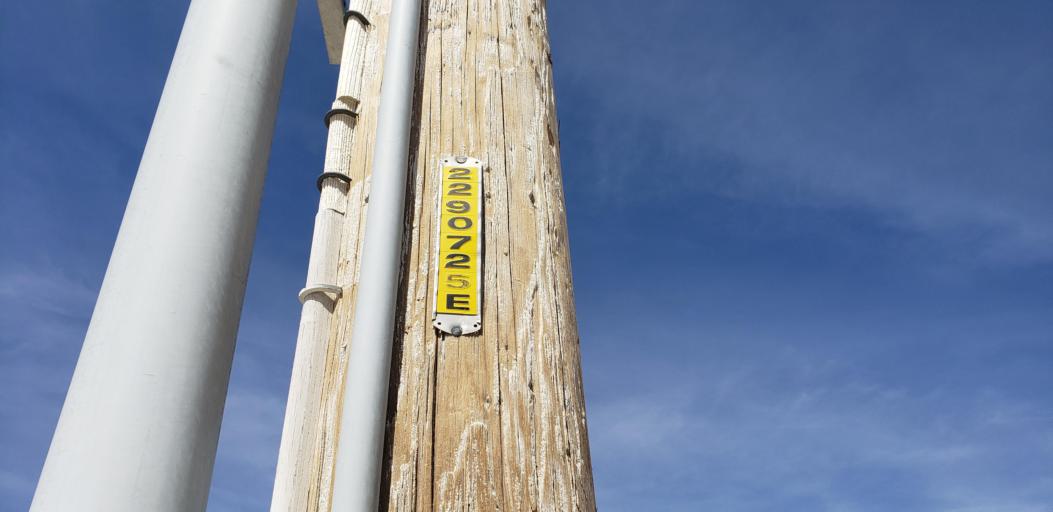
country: US
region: California
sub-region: San Bernardino County
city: Lucerne Valley
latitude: 34.3691
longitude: -116.9064
